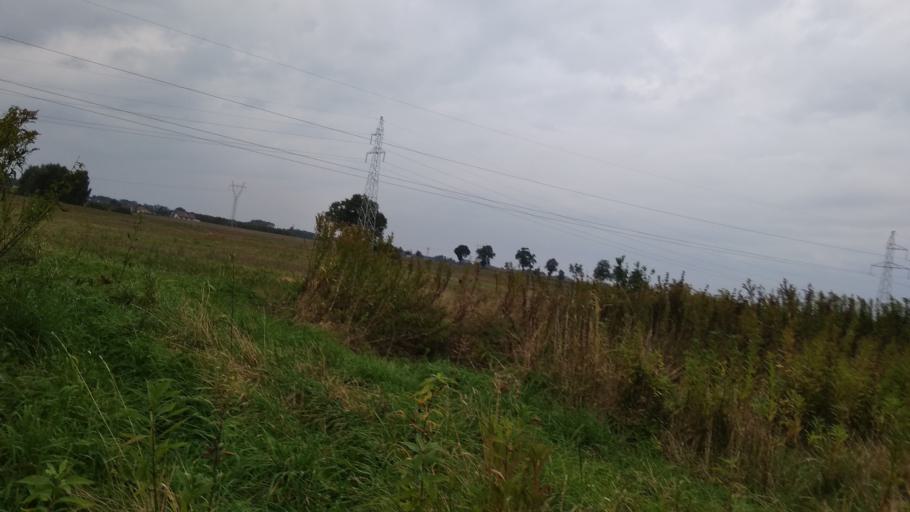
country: PL
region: Kujawsko-Pomorskie
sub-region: Powiat bydgoski
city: Osielsko
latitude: 53.2116
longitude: 18.1447
